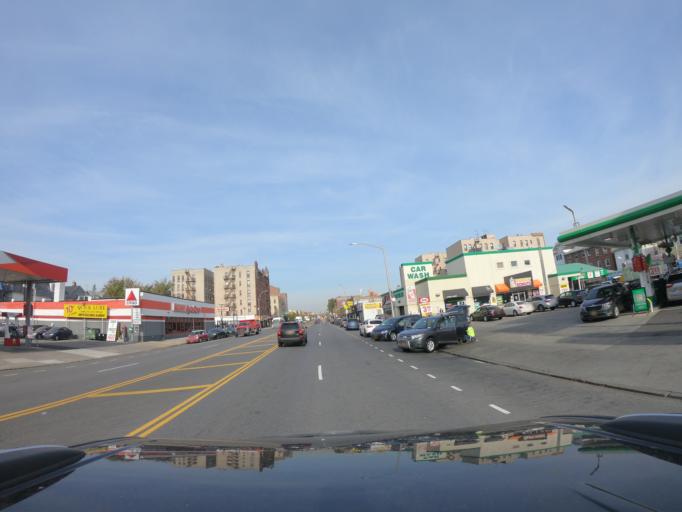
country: US
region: New York
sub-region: Kings County
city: Bensonhurst
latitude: 40.6140
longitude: -73.9631
